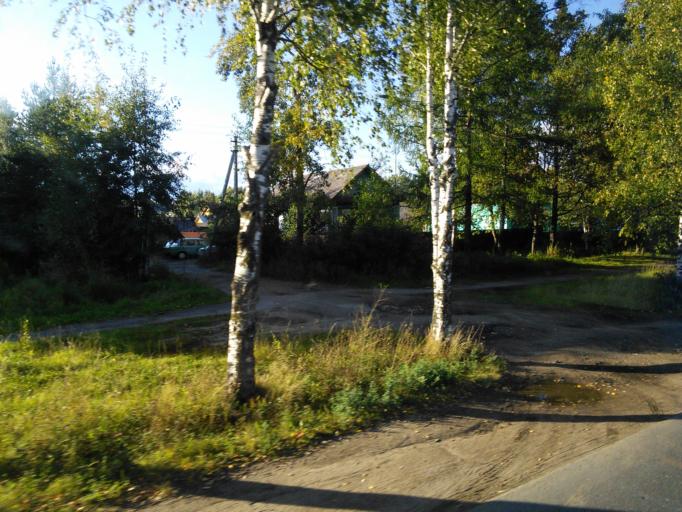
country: RU
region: Jaroslavl
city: Poshekhon'ye
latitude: 58.5003
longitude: 39.1297
